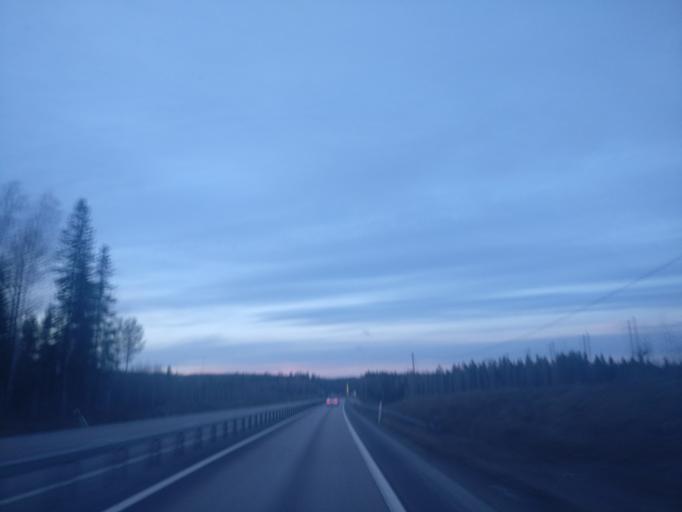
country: FI
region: Central Finland
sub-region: Jyvaeskylae
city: Saeynaetsalo
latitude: 62.2176
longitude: 25.8928
